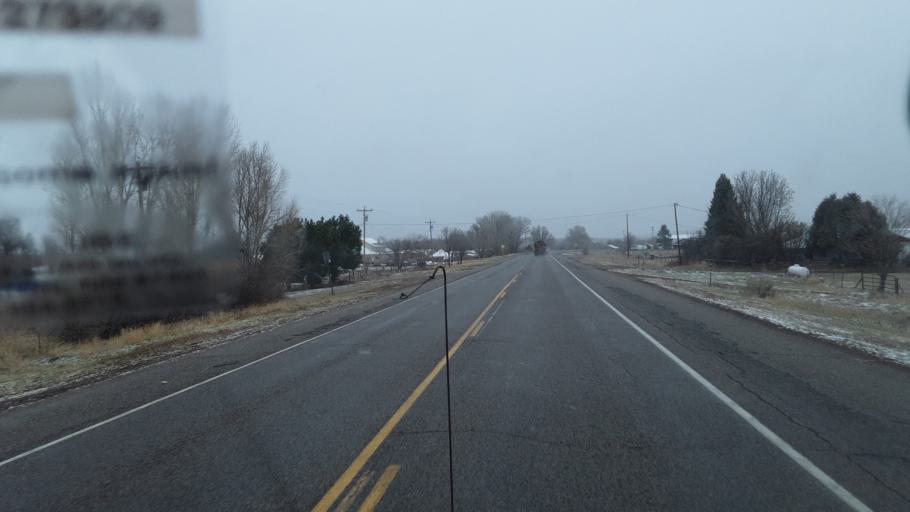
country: US
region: New Mexico
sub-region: Rio Arriba County
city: Tierra Amarilla
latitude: 36.7403
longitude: -106.5688
